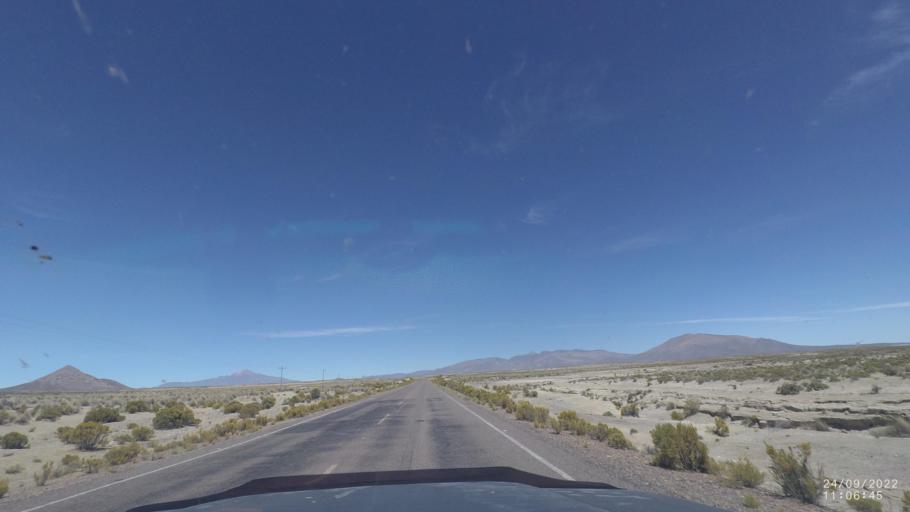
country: BO
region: Oruro
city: Challapata
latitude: -19.4781
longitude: -67.4327
